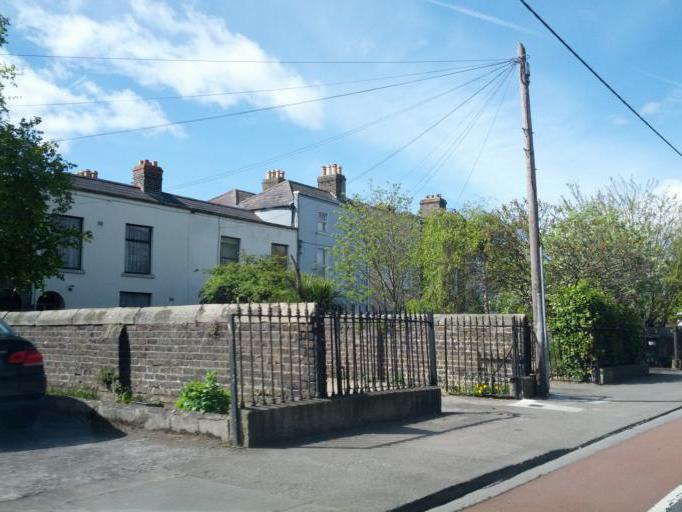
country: IE
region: Leinster
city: Rathgar
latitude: 53.3298
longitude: -6.2785
